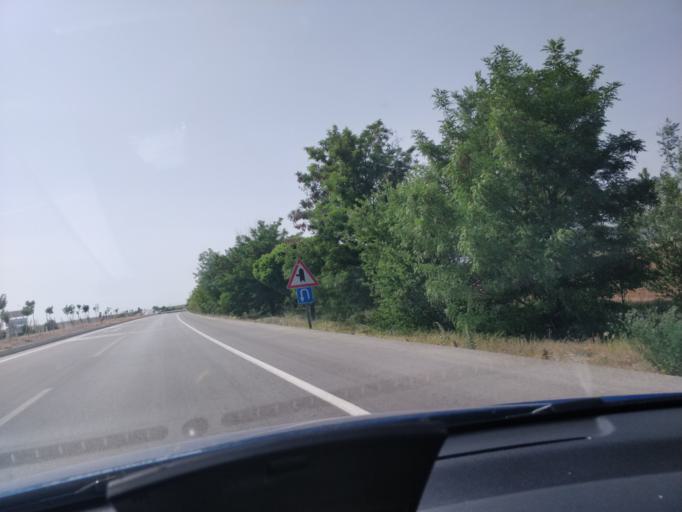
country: TR
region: Konya
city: Guneysinir
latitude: 37.3487
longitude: 32.8098
